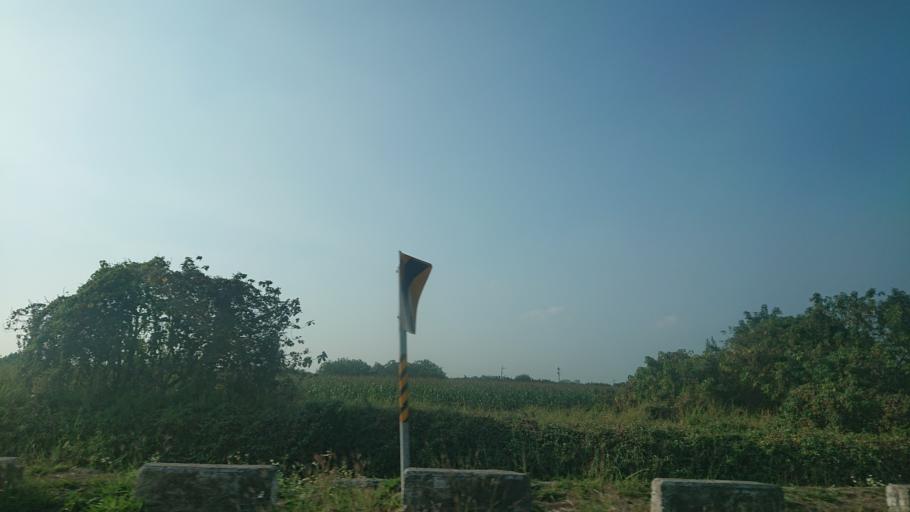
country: TW
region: Taiwan
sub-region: Tainan
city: Tainan
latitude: 23.1409
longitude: 120.2436
